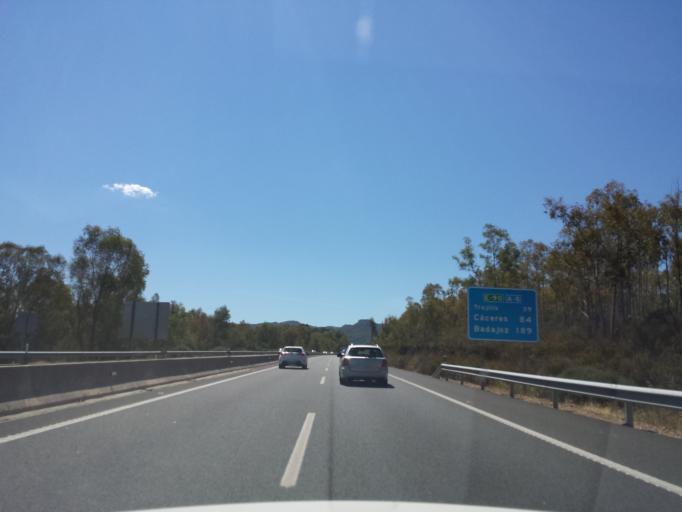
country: ES
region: Extremadura
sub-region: Provincia de Caceres
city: Romangordo
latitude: 39.7248
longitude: -5.7143
